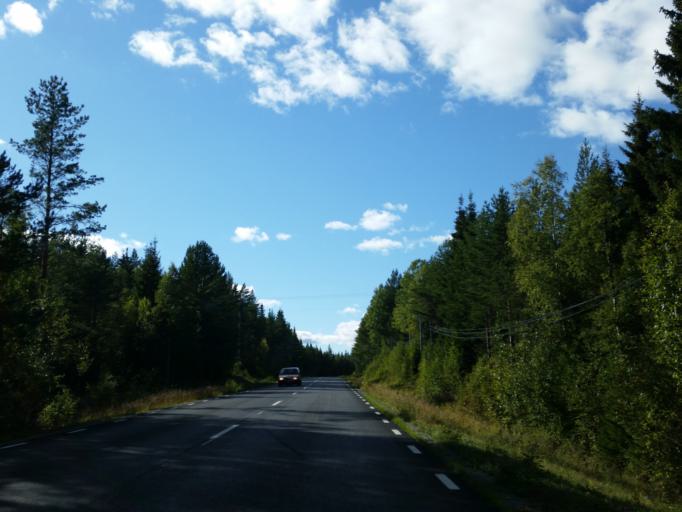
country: SE
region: Vaesterbotten
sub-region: Robertsfors Kommun
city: Robertsfors
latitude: 64.1598
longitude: 20.9489
